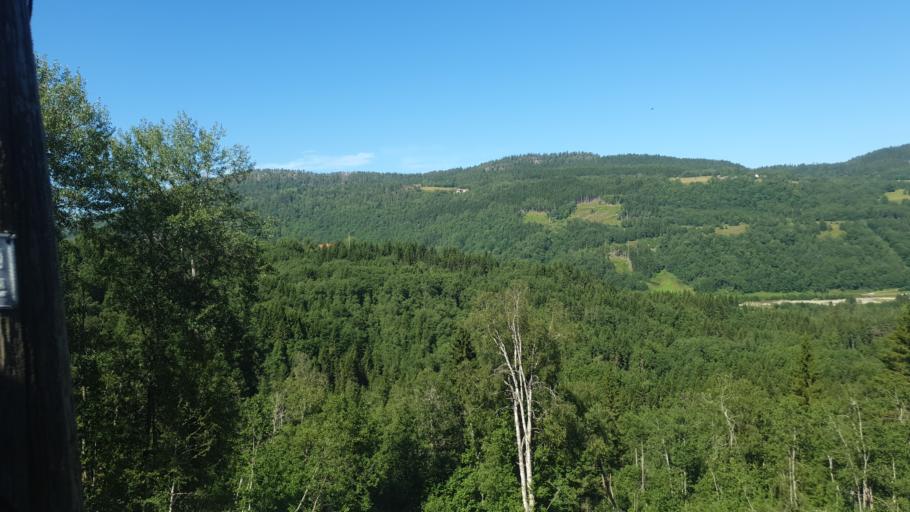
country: NO
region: Sor-Trondelag
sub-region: Meldal
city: Meldal
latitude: 63.1551
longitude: 9.7236
